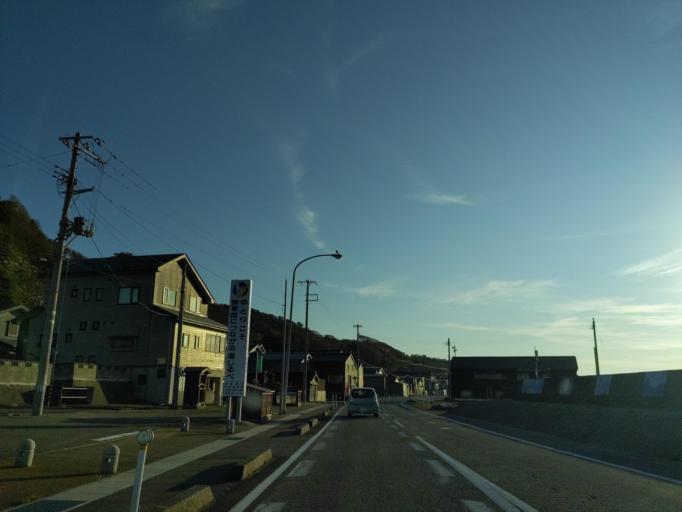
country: JP
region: Niigata
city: Nagaoka
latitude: 37.5433
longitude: 138.6865
